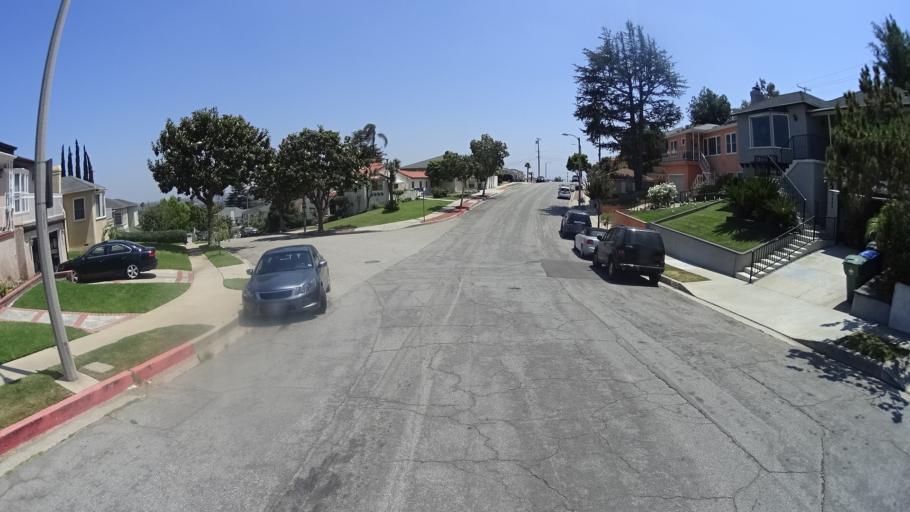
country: US
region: California
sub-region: Los Angeles County
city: View Park-Windsor Hills
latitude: 33.9921
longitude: -118.3529
